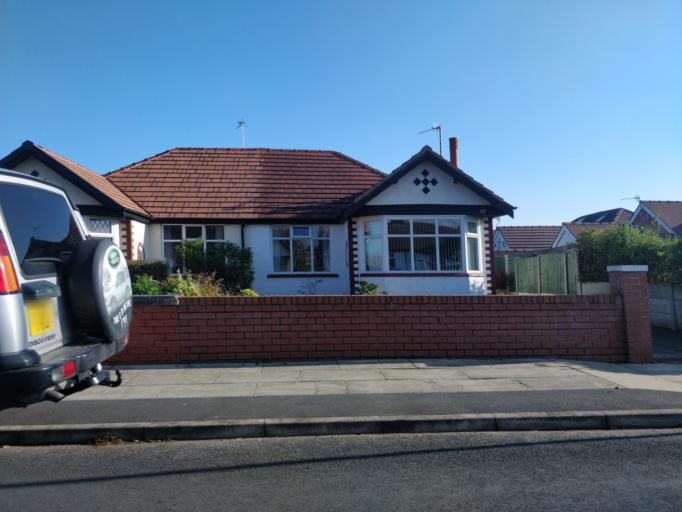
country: GB
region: England
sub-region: Lancashire
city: Banks
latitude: 53.6687
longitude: -2.9622
